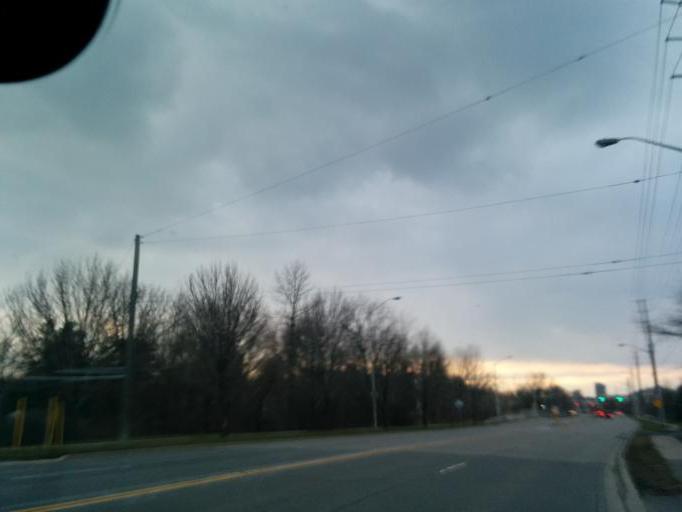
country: CA
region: Ontario
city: Oakville
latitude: 43.4607
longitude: -79.6743
